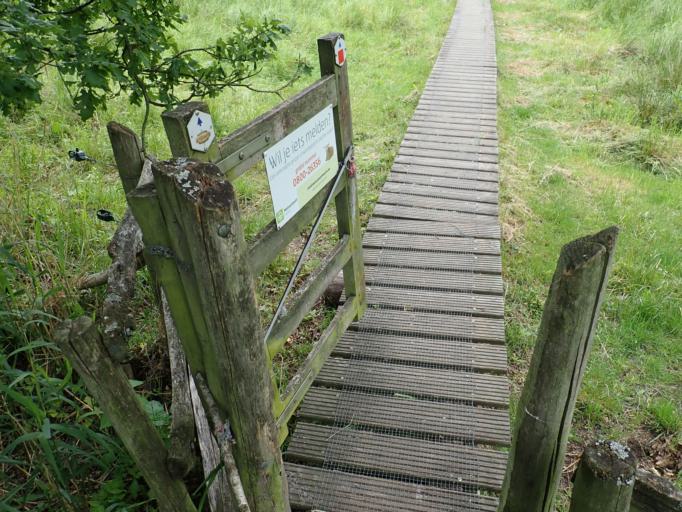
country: BE
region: Flanders
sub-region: Provincie Vlaams-Brabant
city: Haacht
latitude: 50.9634
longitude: 4.6544
